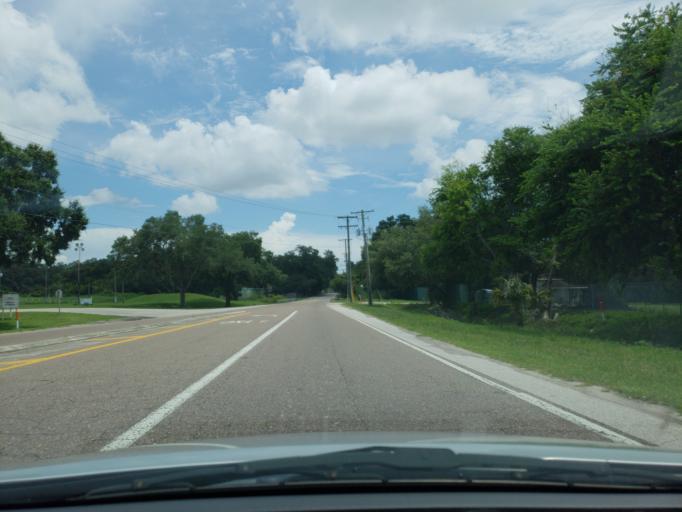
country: US
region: Florida
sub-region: Hillsborough County
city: East Lake-Orient Park
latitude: 27.9884
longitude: -82.3731
